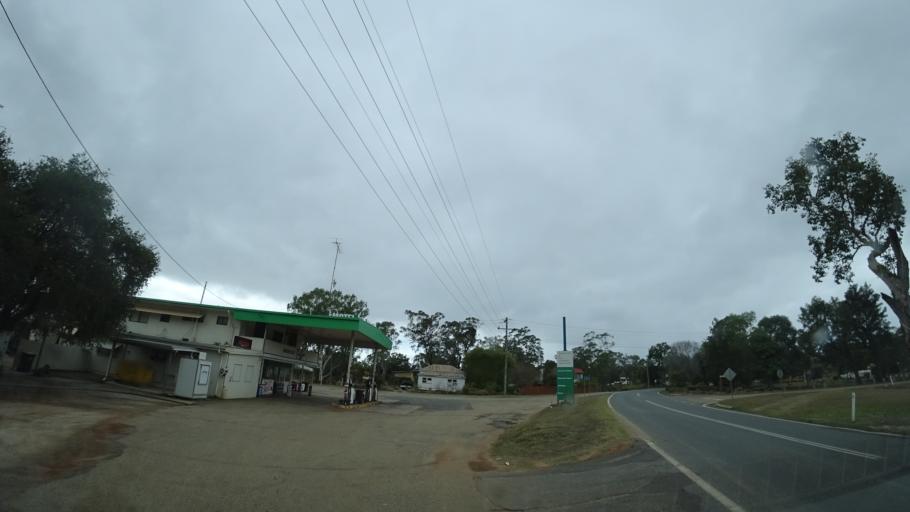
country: AU
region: Queensland
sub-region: Tablelands
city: Ravenshoe
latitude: -17.6755
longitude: 145.1122
